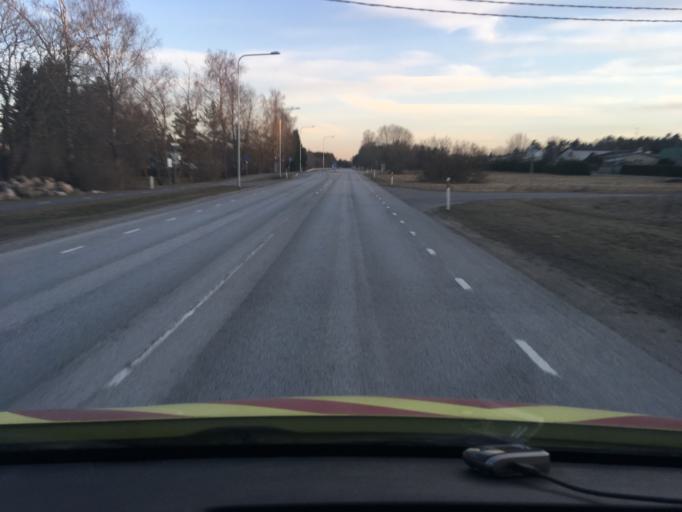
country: EE
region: Harju
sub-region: Kiili vald
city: Kiili
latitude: 59.3407
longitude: 24.7740
